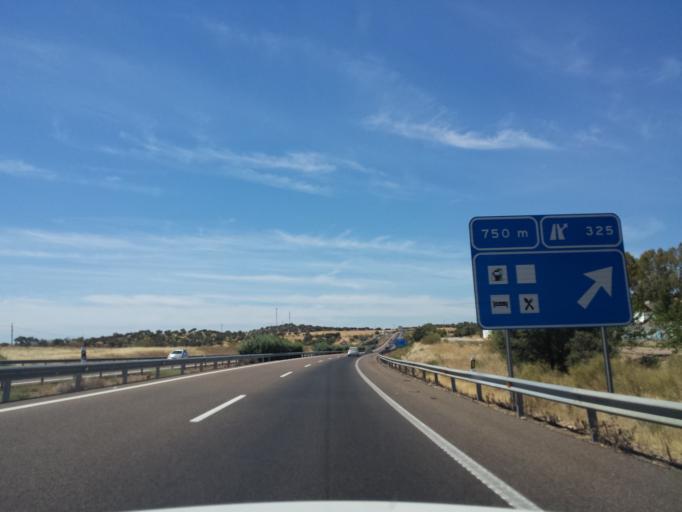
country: ES
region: Extremadura
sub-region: Provincia de Badajoz
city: San Pedro de Merida
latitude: 38.9512
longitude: -6.1671
